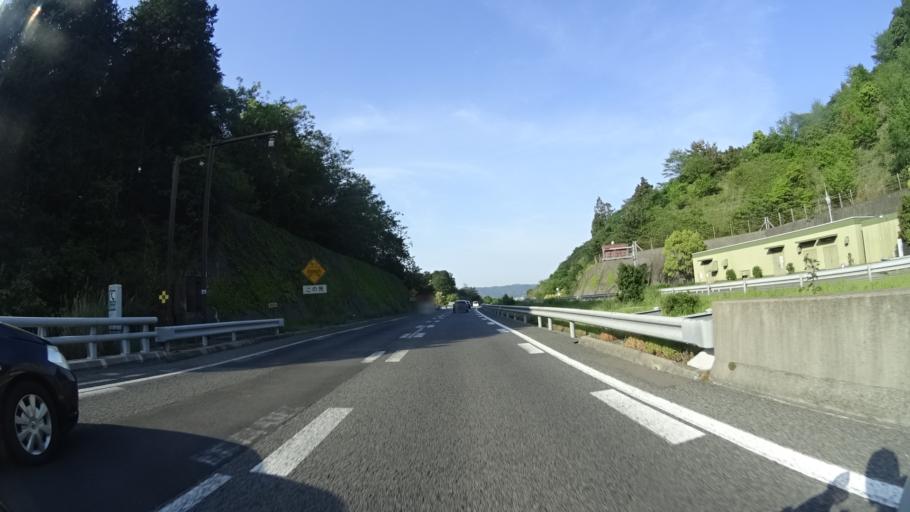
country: JP
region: Ehime
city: Saijo
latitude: 33.9015
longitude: 133.2007
